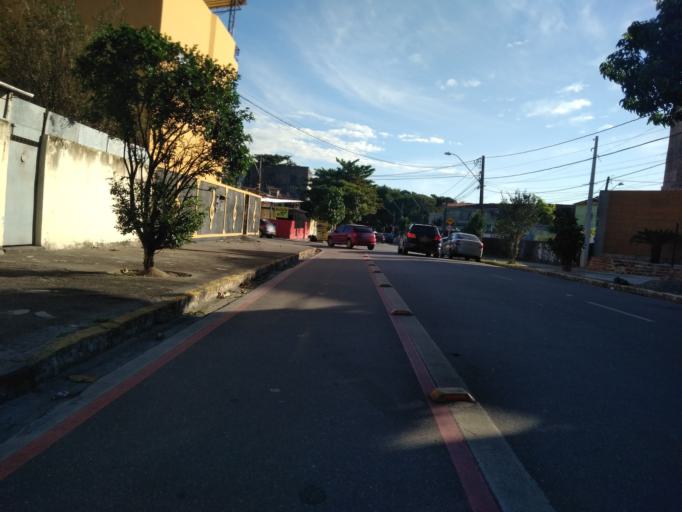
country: BR
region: Pernambuco
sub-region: Recife
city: Recife
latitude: -8.0808
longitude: -34.9368
